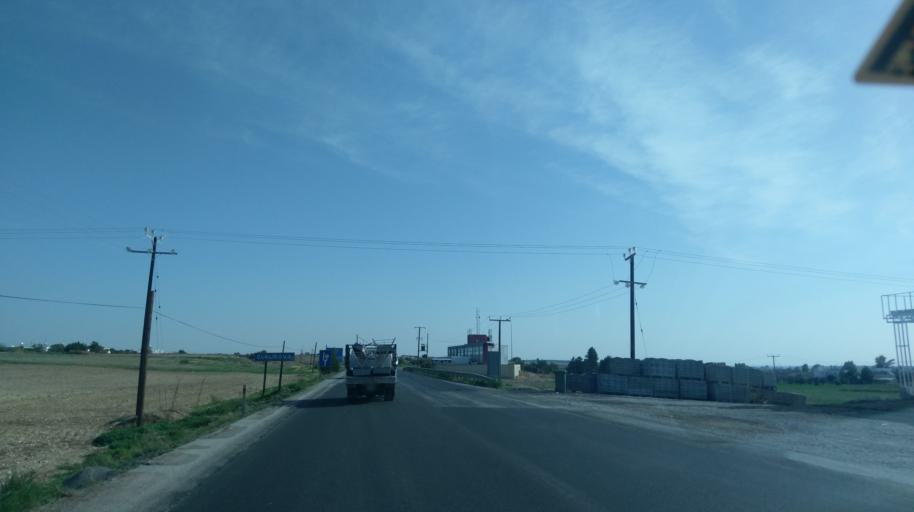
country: CY
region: Larnaka
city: Athienou
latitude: 35.2297
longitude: 33.5507
